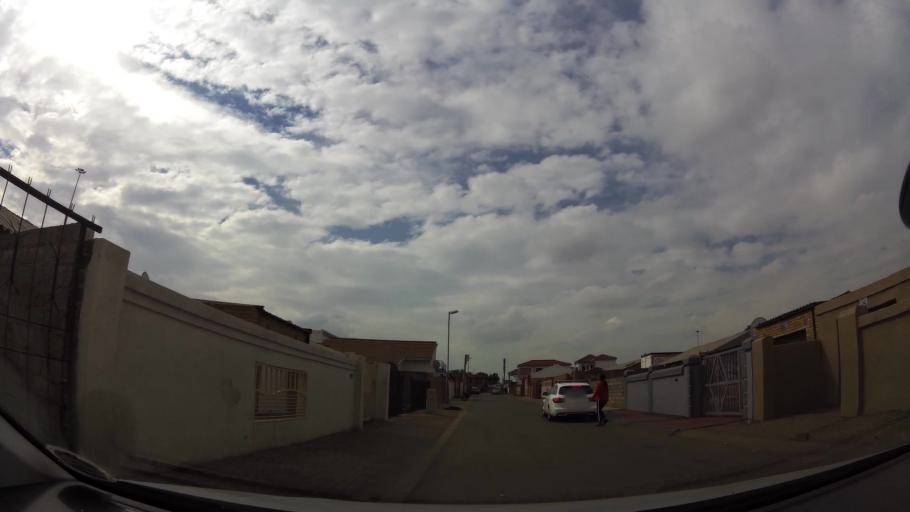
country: ZA
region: Gauteng
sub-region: City of Johannesburg Metropolitan Municipality
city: Soweto
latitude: -26.2674
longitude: 27.8540
